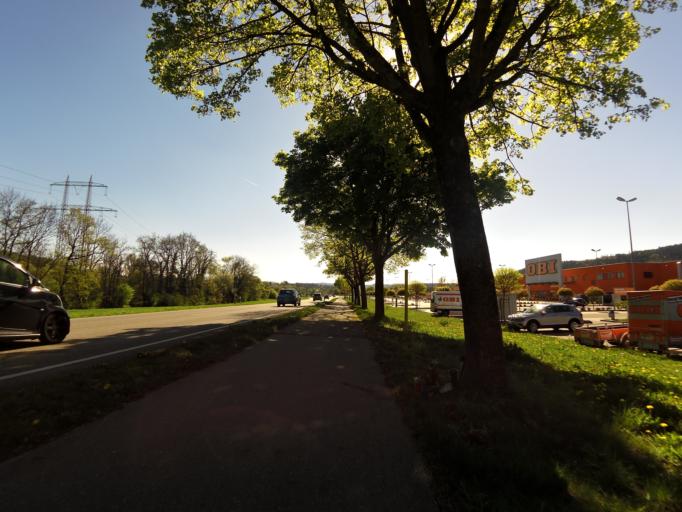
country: CH
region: Aargau
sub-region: Bezirk Zurzach
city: Koblenz
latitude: 47.6180
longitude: 8.2511
